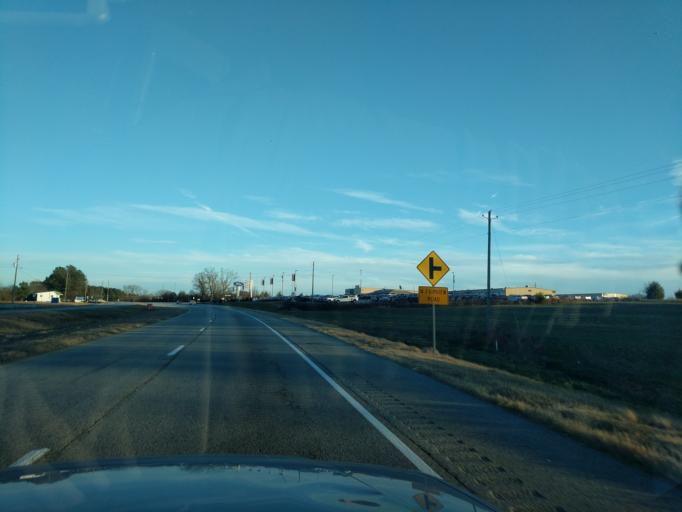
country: US
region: Georgia
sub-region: Franklin County
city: Lavonia
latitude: 34.4493
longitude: -83.1449
